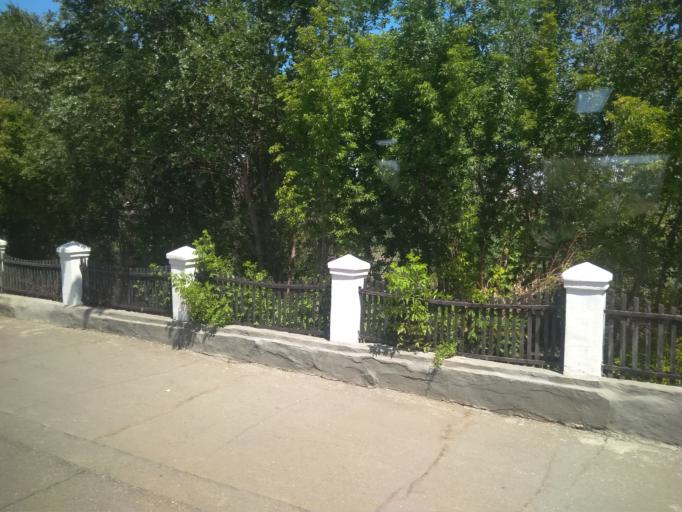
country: RU
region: Volgograd
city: Krasnoslobodsk
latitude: 48.5188
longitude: 44.5131
